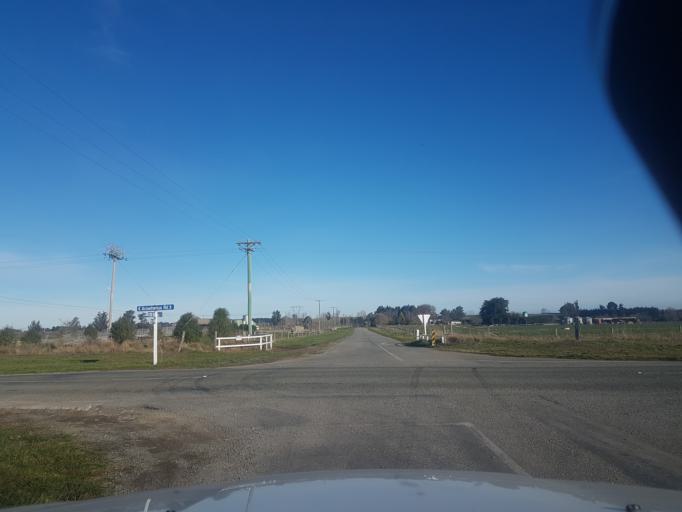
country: NZ
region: Canterbury
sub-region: Timaru District
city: Pleasant Point
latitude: -44.2708
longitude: 171.1718
